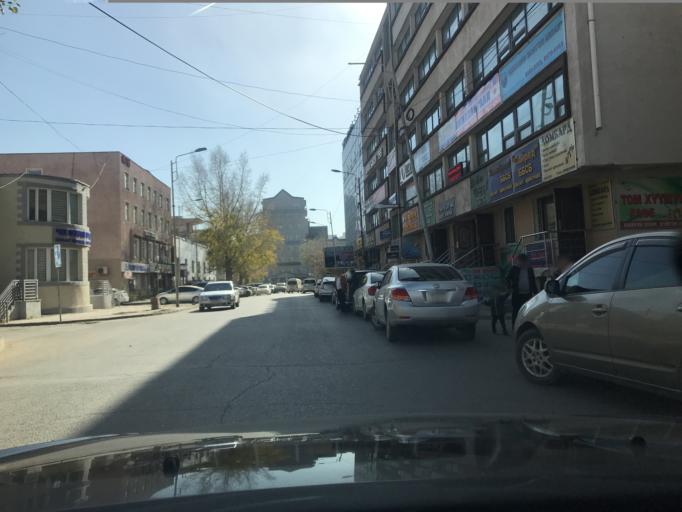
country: MN
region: Ulaanbaatar
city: Ulaanbaatar
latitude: 47.9207
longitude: 106.9028
